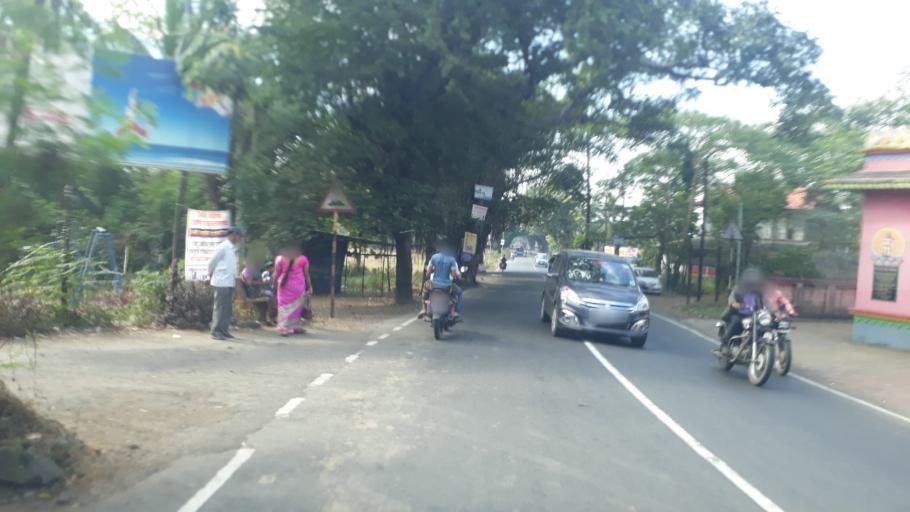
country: IN
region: Maharashtra
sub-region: Raigarh
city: Alibag
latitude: 18.6765
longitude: 72.9158
